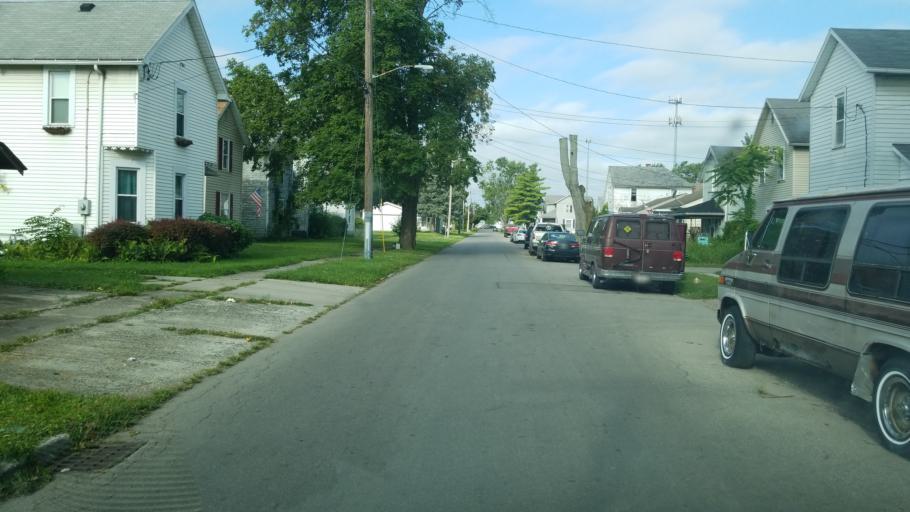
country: US
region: Ohio
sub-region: Marion County
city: Marion
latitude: 40.5903
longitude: -83.1158
